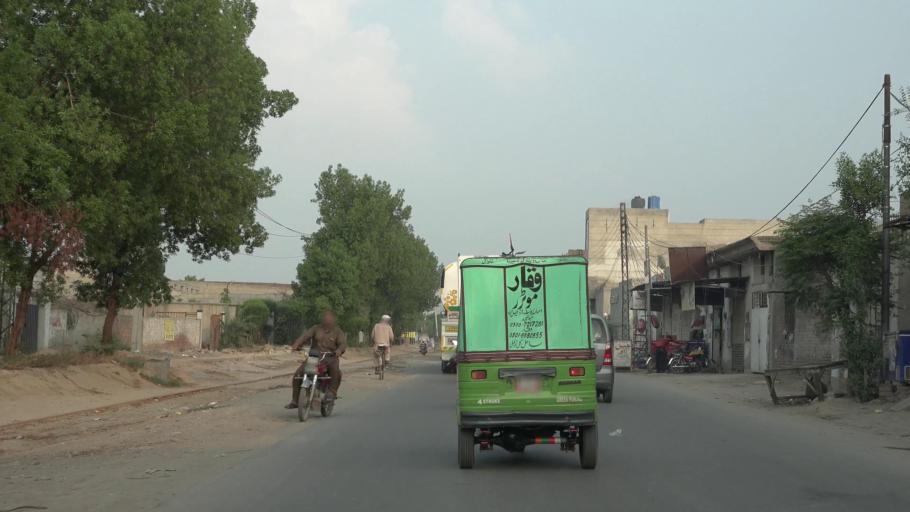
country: PK
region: Punjab
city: Faisalabad
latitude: 31.4500
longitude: 73.1228
